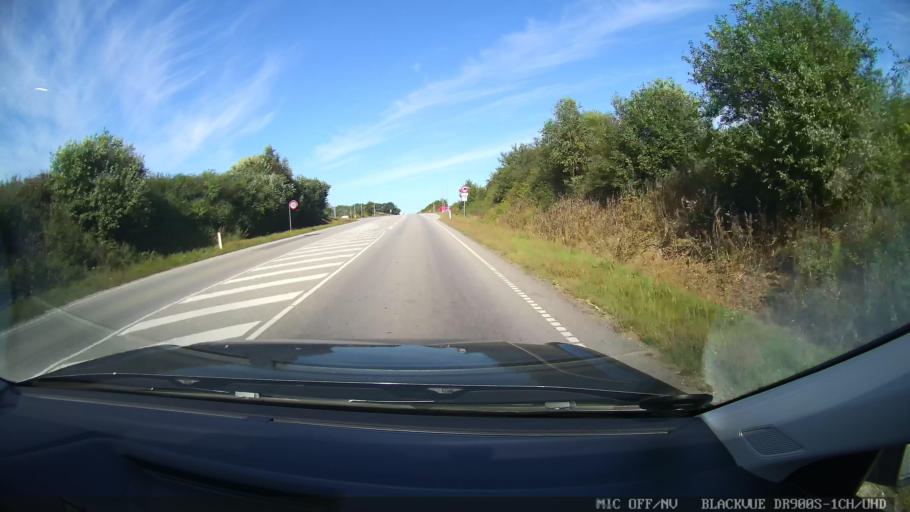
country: DK
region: North Denmark
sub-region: Mariagerfjord Kommune
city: Hobro
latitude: 56.6606
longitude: 9.7828
